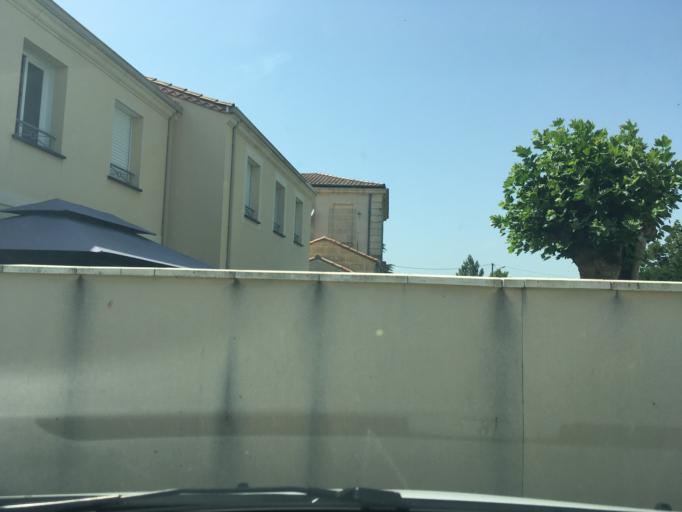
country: FR
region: Aquitaine
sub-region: Departement de la Gironde
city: Cantenac
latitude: 45.0151
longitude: -0.6397
